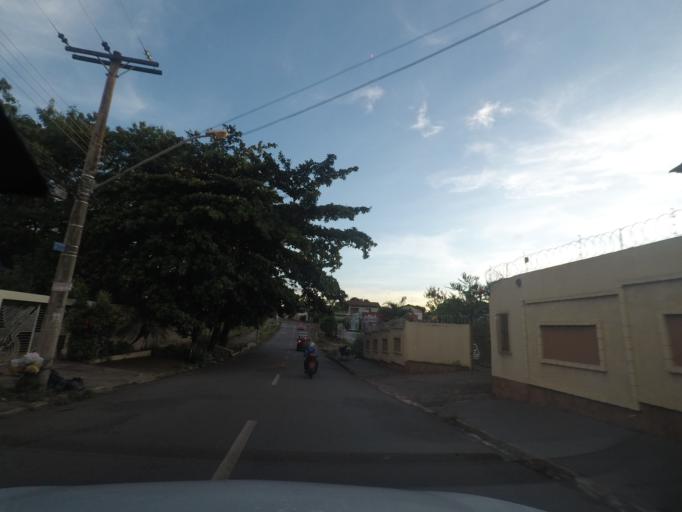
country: BR
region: Goias
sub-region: Goiania
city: Goiania
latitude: -16.6924
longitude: -49.2856
